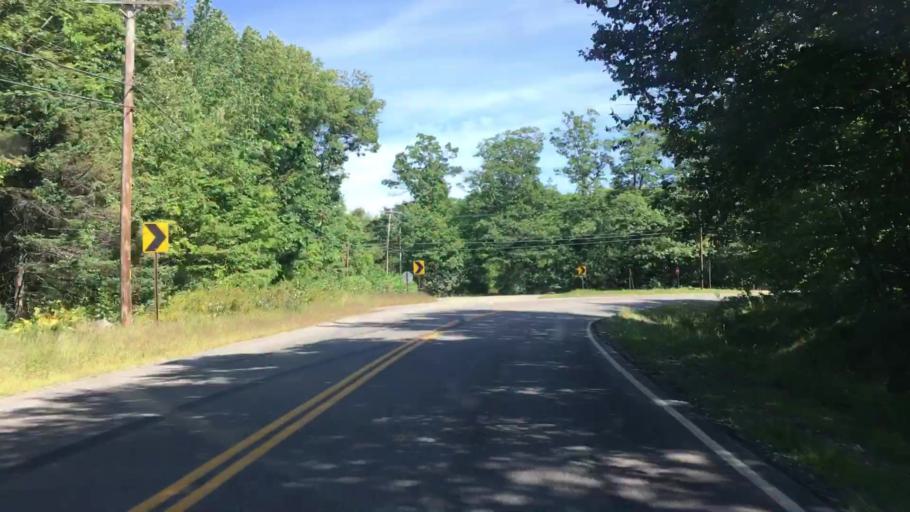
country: US
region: Maine
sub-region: Penobscot County
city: Bradford
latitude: 45.1772
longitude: -68.8552
